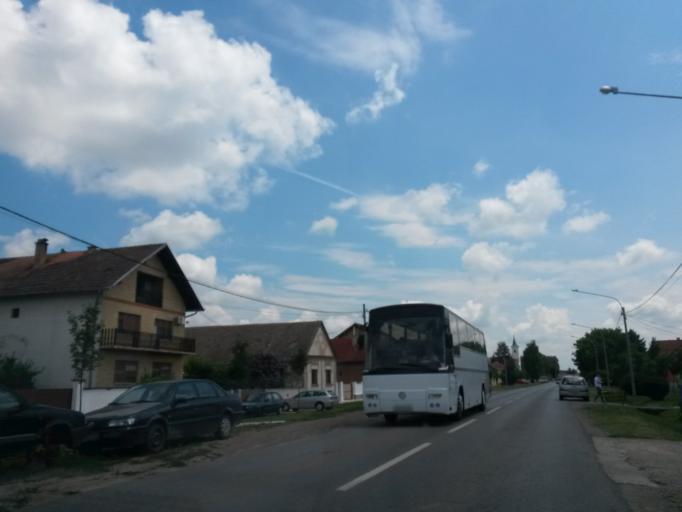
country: HR
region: Osjecko-Baranjska
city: Sarvas
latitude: 45.5260
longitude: 18.8382
